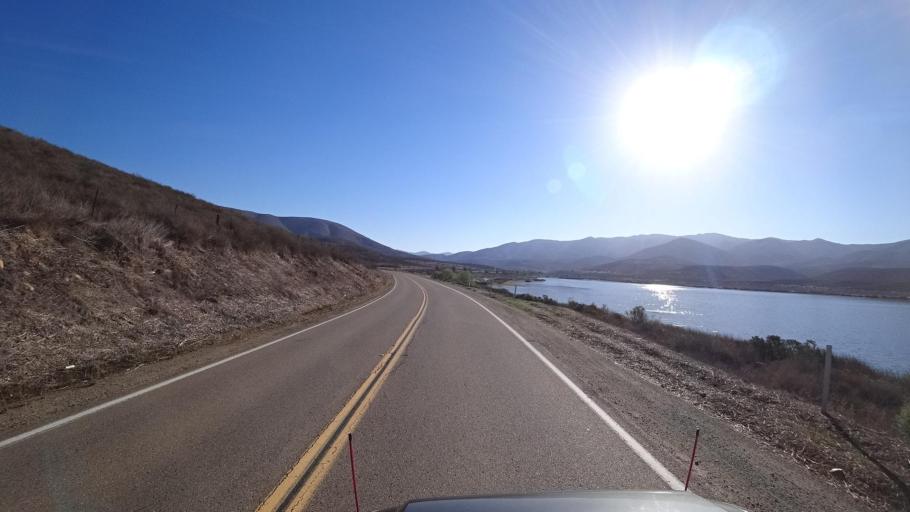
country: US
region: California
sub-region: San Diego County
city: Jamul
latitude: 32.6340
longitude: -116.9155
